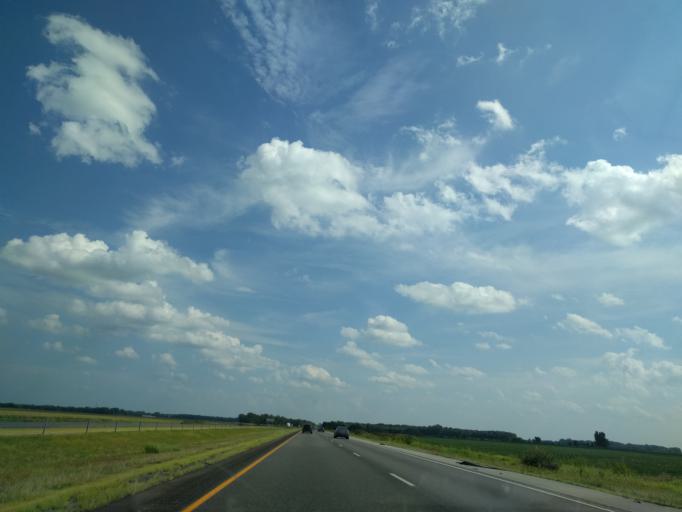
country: US
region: Indiana
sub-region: Jasper County
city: Rensselaer
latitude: 40.8562
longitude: -87.1829
